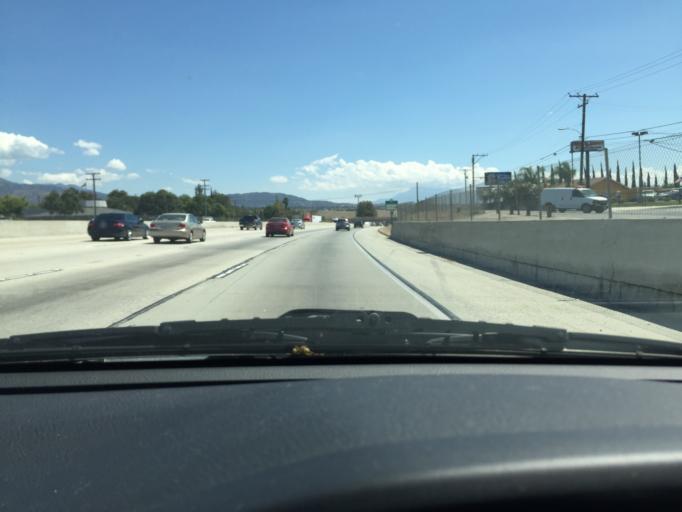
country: US
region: California
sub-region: Riverside County
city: Calimesa
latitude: 34.0235
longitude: -117.1079
